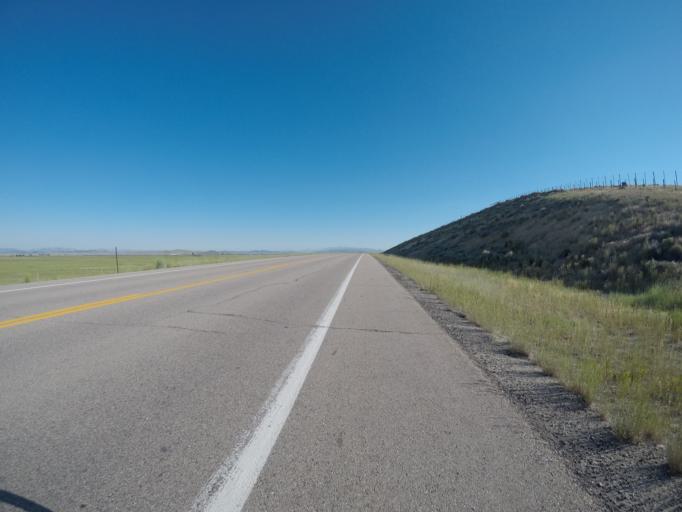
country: US
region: Wyoming
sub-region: Sublette County
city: Pinedale
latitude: 42.9436
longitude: -110.0837
